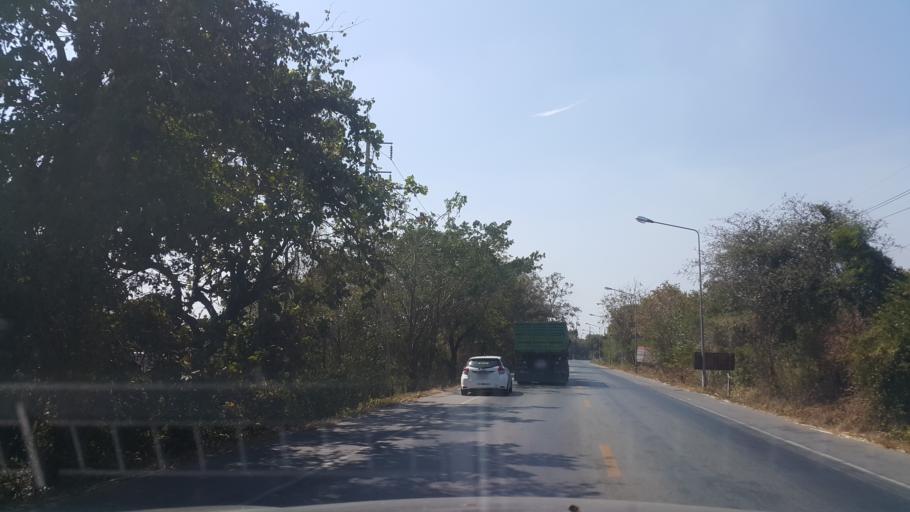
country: TH
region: Nakhon Ratchasima
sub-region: Amphoe Kaeng Sanam Nang
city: Kaeng Sanam Nang
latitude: 15.7547
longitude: 102.2465
